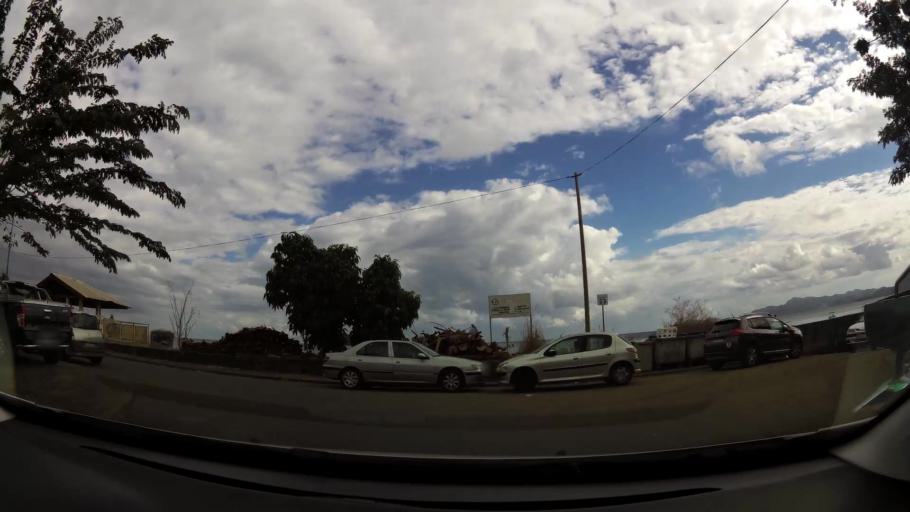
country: YT
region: Sada
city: Sada
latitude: -12.8497
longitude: 45.0985
